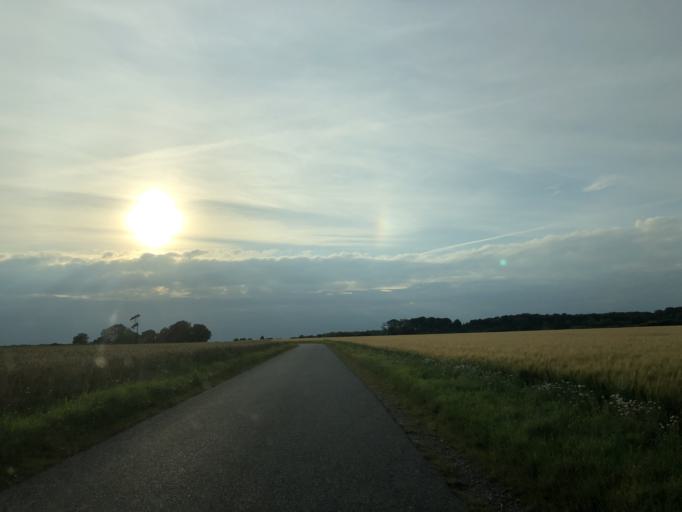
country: DK
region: South Denmark
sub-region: Fredericia Kommune
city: Taulov
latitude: 55.5949
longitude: 9.6102
